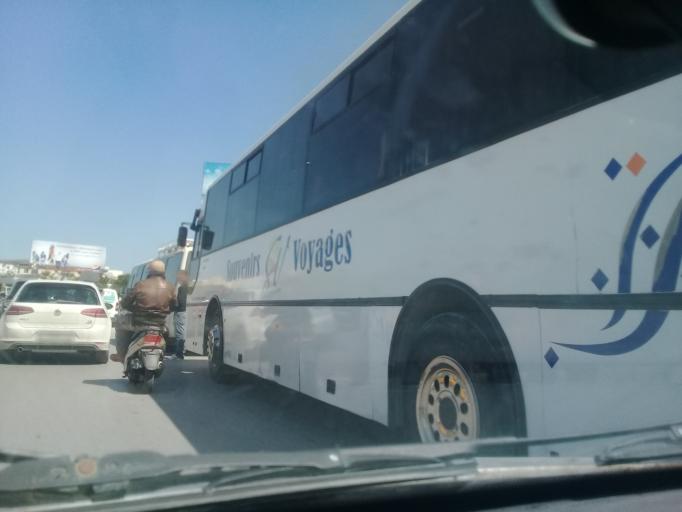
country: TN
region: Ariana
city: Ariana
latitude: 36.8332
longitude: 10.2318
